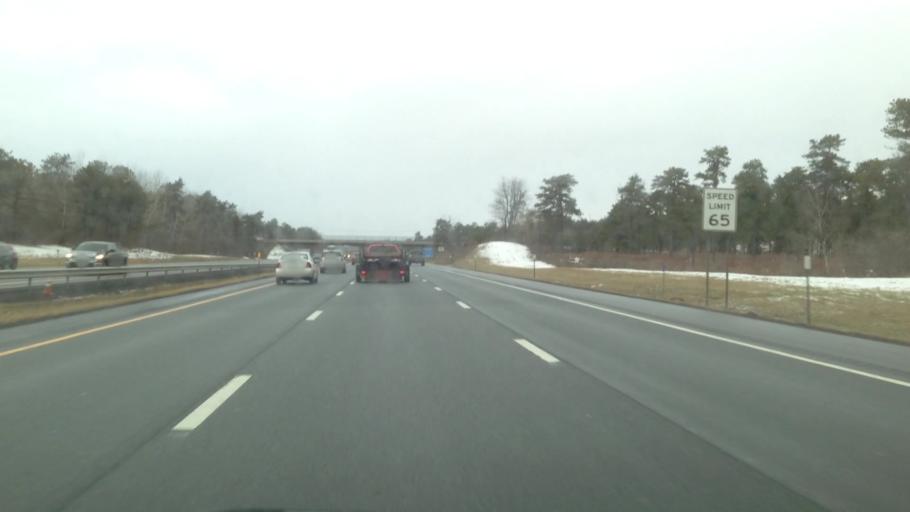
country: US
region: New York
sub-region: Albany County
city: Westmere
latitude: 42.7123
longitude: -73.8655
